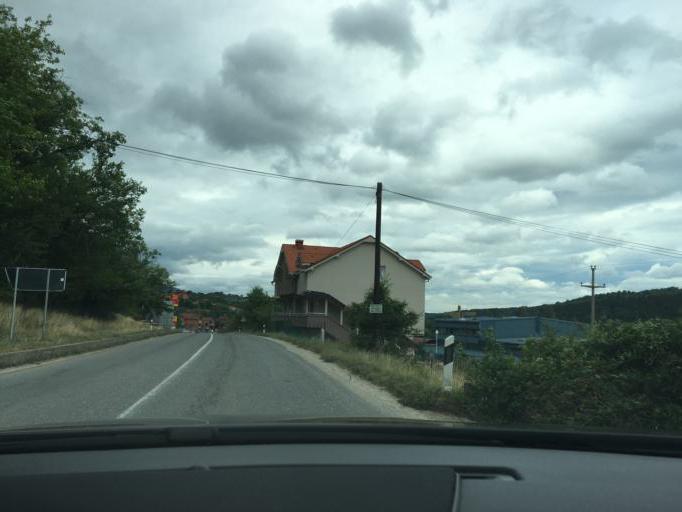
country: MK
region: Kriva Palanka
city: Kriva Palanka
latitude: 42.1904
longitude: 22.3050
